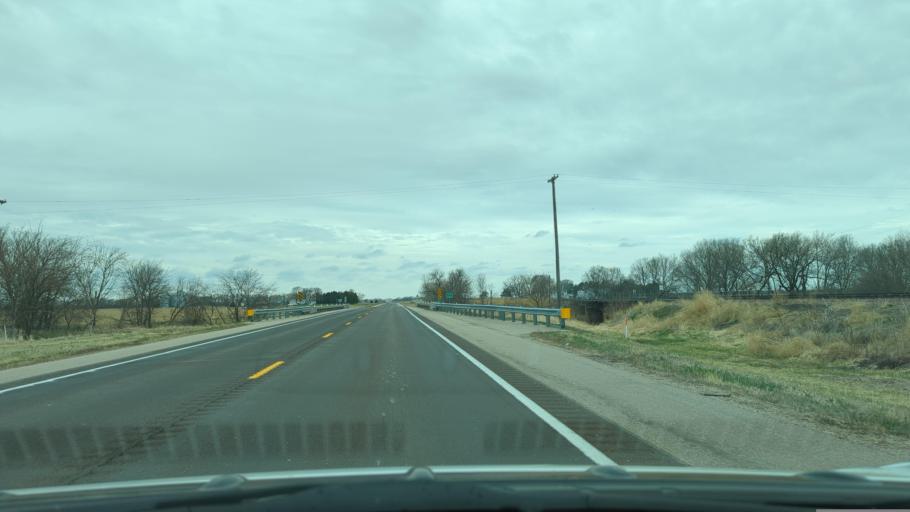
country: US
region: Nebraska
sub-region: Lancaster County
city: Waverly
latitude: 40.9395
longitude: -96.4816
